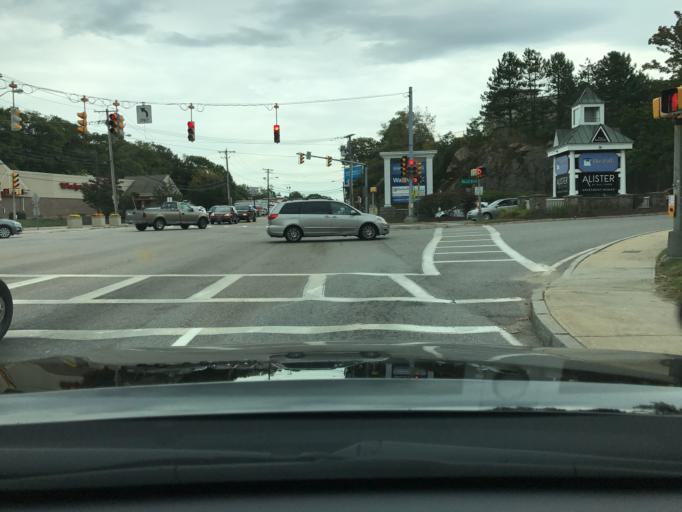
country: US
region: Massachusetts
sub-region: Norfolk County
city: Quincy
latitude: 42.2392
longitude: -70.9845
